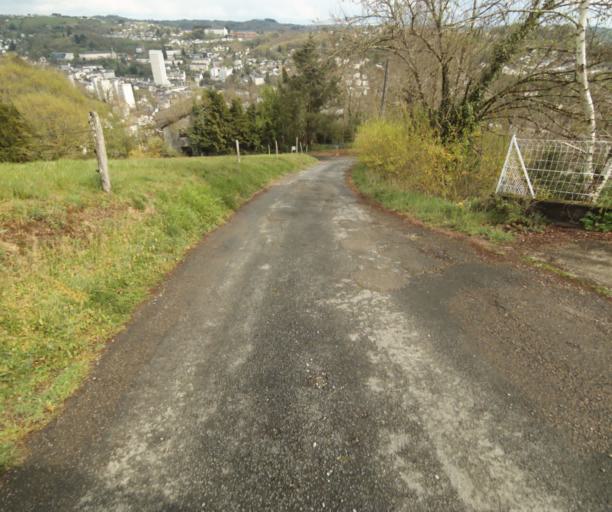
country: FR
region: Limousin
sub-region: Departement de la Correze
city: Tulle
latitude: 45.2642
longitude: 1.7559
